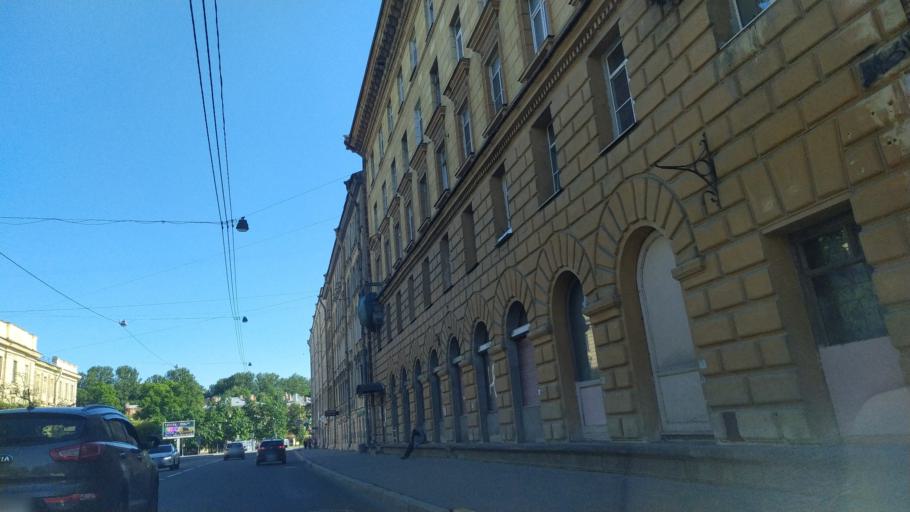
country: RU
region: Leningrad
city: Finlyandskiy
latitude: 59.9609
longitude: 30.3450
